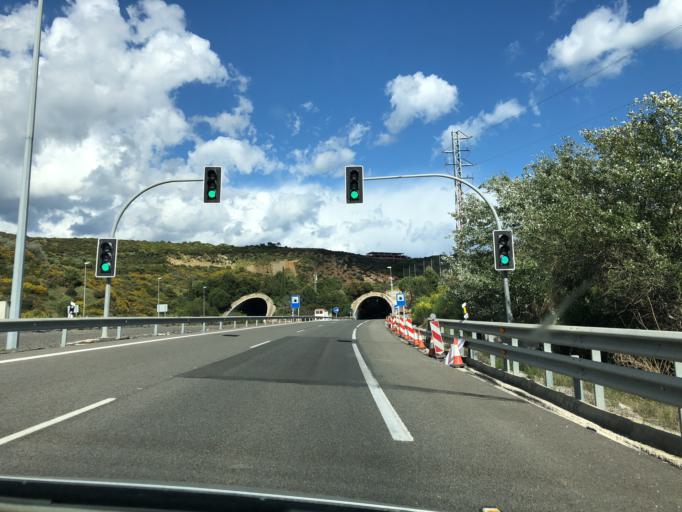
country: ES
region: Andalusia
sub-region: Provincia de Malaga
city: Manilva
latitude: 36.4014
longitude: -5.2447
